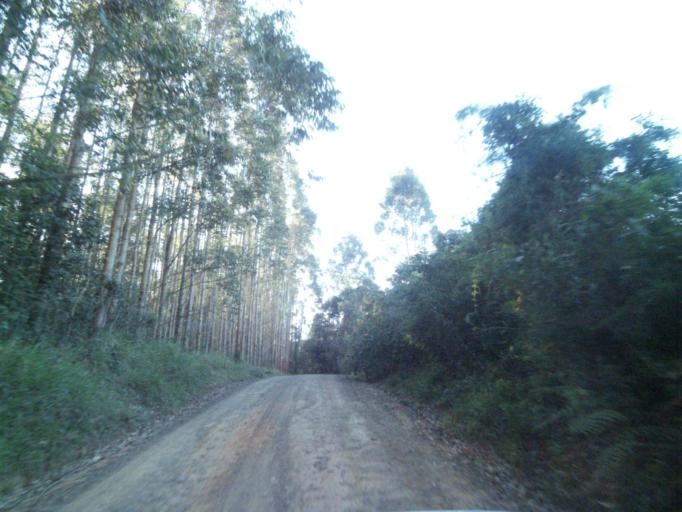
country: BR
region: Parana
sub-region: Telemaco Borba
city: Telemaco Borba
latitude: -24.5031
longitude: -50.5981
